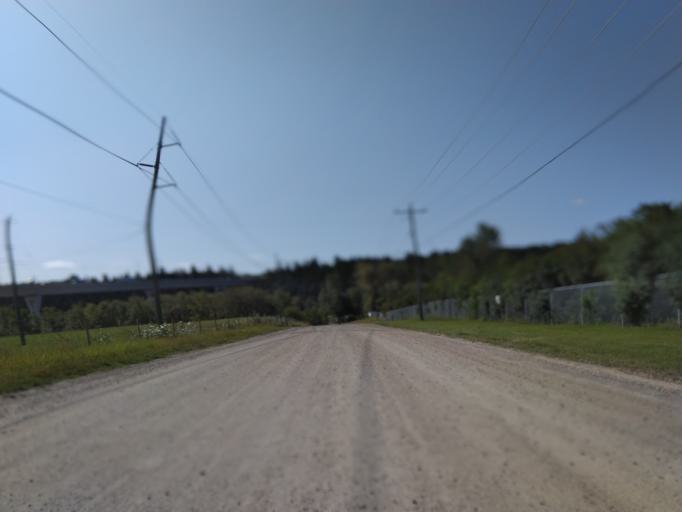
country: CA
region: Alberta
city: Calgary
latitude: 51.1017
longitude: -114.2342
